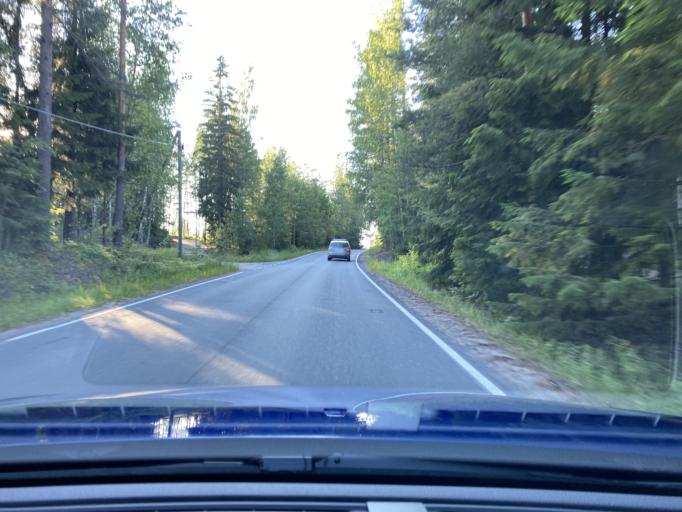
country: FI
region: Haeme
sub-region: Riihimaeki
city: Riihimaeki
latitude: 60.7264
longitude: 24.6964
